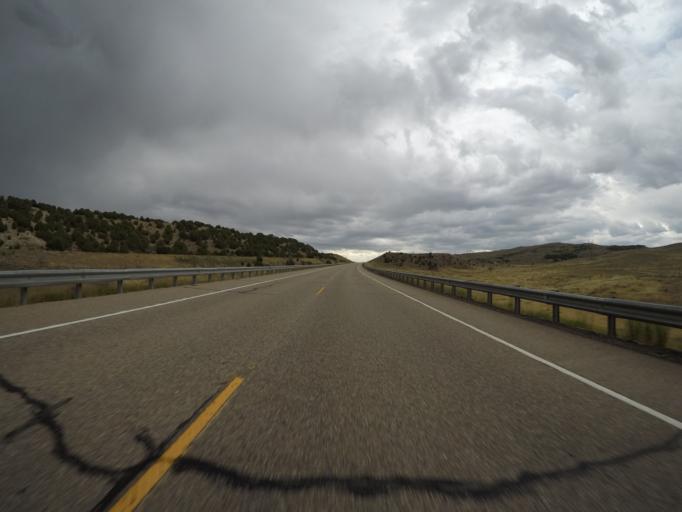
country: US
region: Colorado
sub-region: Rio Blanco County
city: Rangely
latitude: 40.3677
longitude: -108.4061
